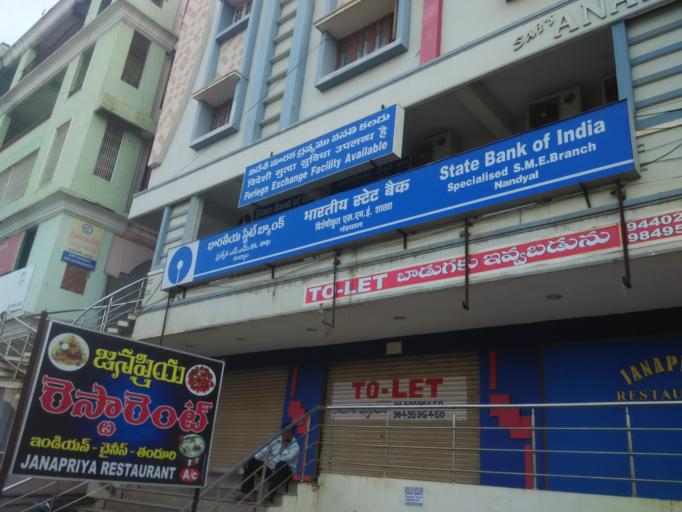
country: IN
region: Andhra Pradesh
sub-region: Kurnool
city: Nandyal
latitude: 15.4831
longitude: 78.4849
